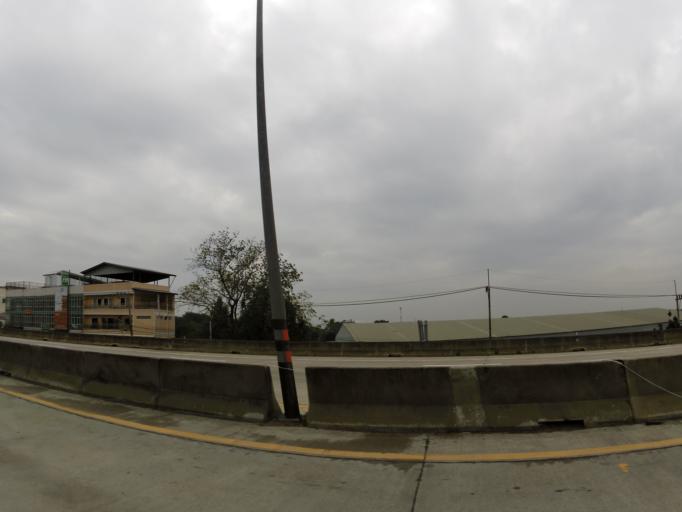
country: TH
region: Chon Buri
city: Si Racha
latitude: 13.1112
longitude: 100.9499
